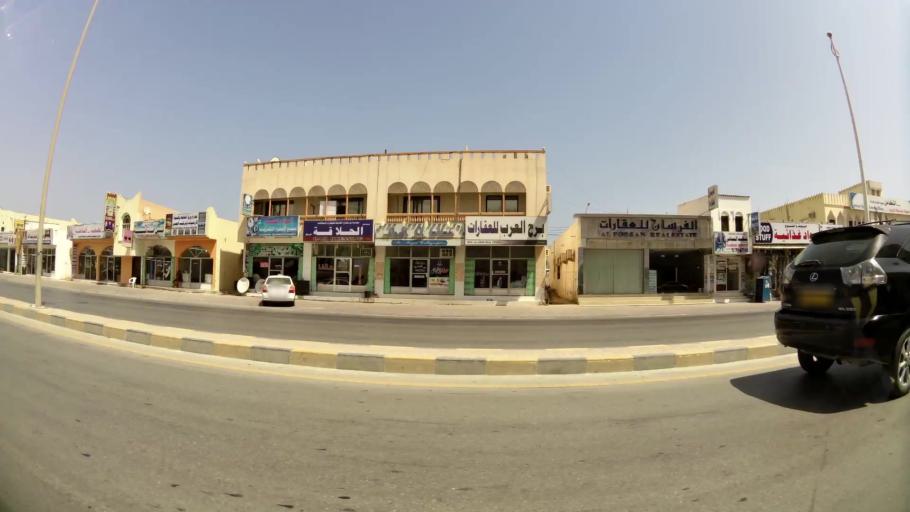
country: OM
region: Zufar
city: Salalah
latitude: 17.0113
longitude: 54.0809
